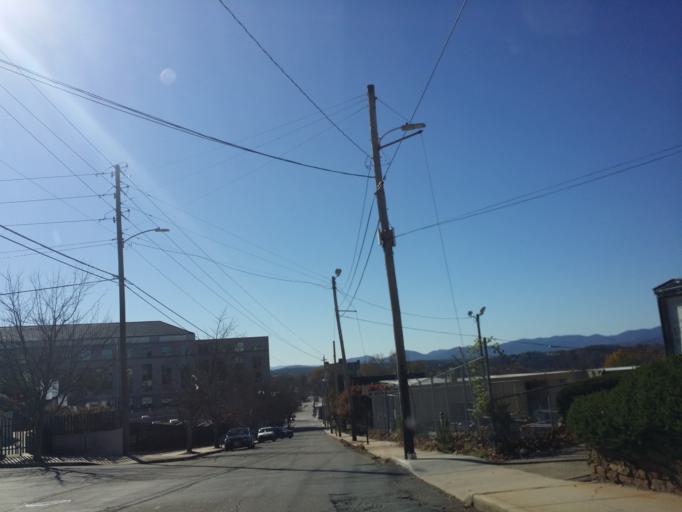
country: US
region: North Carolina
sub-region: Buncombe County
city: Asheville
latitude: 35.5957
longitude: -82.5585
